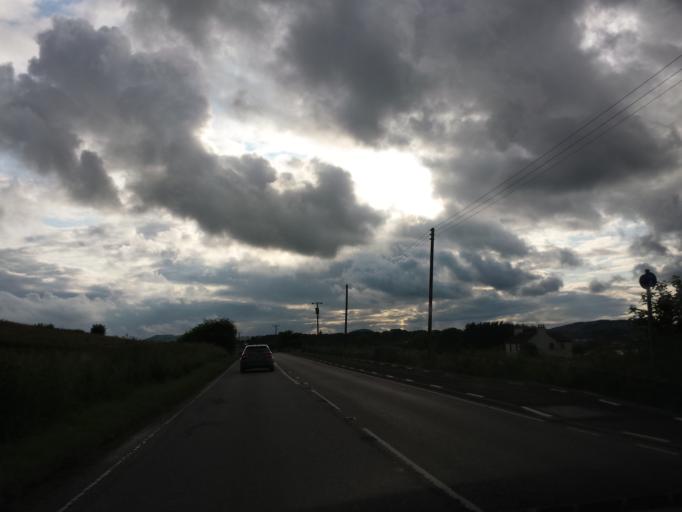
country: GB
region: Scotland
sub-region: Fife
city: Leuchars
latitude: 56.3589
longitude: -2.8709
